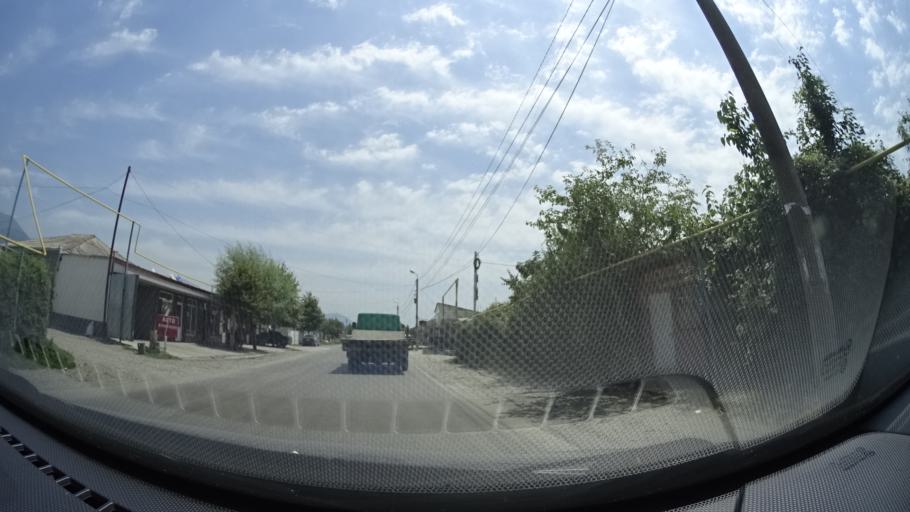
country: GE
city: Bagdadi
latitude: 41.8432
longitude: 46.1331
